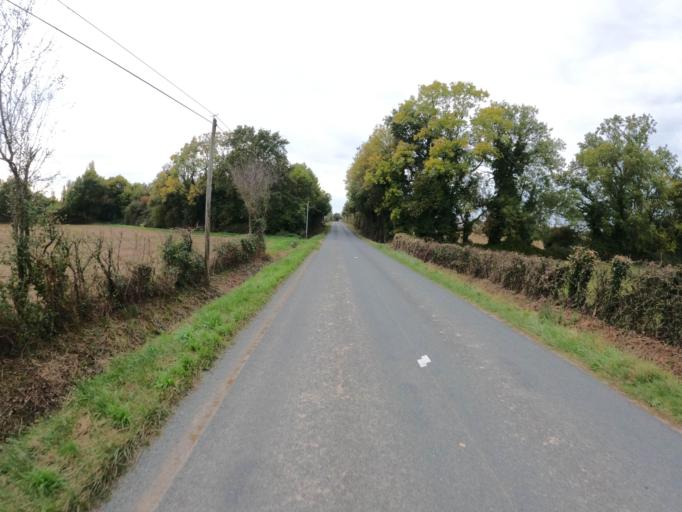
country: FR
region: Pays de la Loire
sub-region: Departement de Maine-et-Loire
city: Saint-Christophe-du-Bois
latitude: 47.0223
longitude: -0.9818
